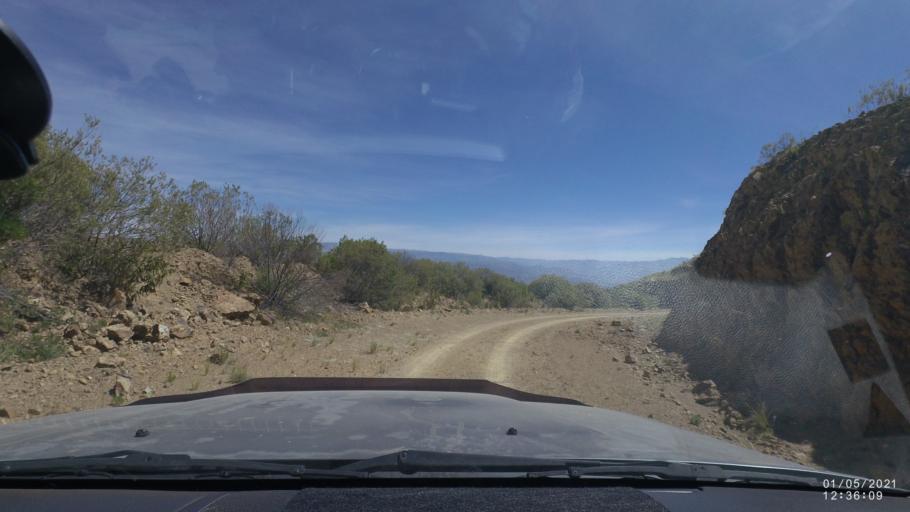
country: BO
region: Cochabamba
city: Capinota
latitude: -17.6787
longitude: -66.1548
